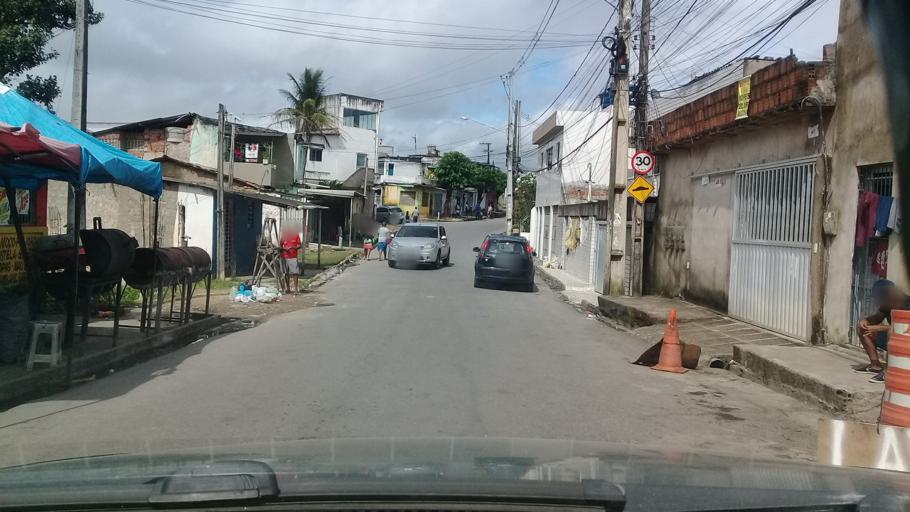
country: BR
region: Pernambuco
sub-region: Jaboatao Dos Guararapes
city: Jaboatao dos Guararapes
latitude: -8.1099
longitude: -34.9633
